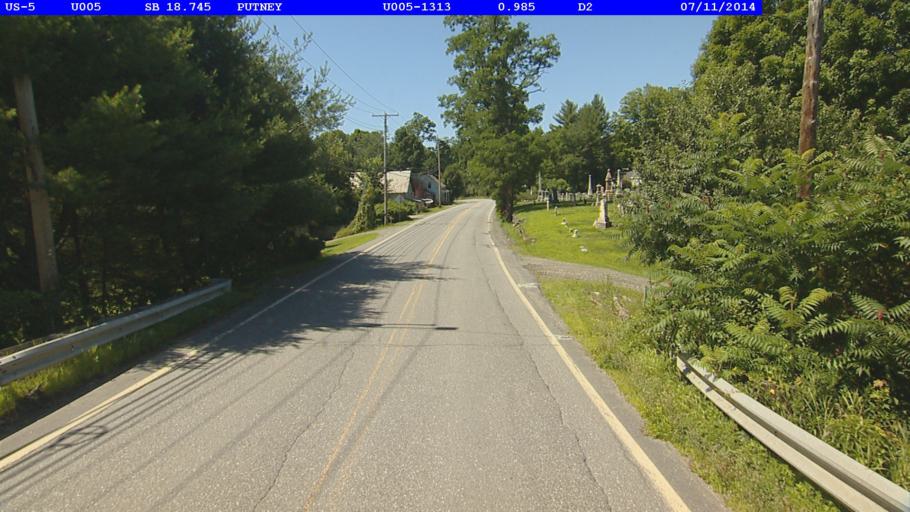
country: US
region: New Hampshire
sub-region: Cheshire County
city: Westmoreland
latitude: 42.9789
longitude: -72.5182
